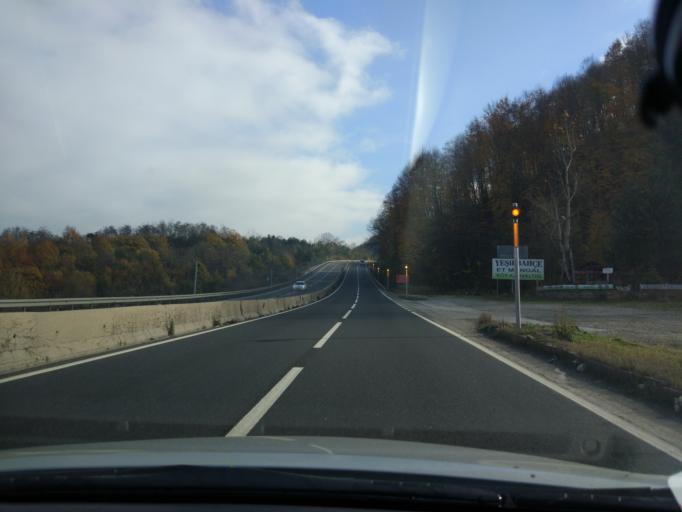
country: TR
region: Duzce
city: Kaynasli
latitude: 40.7579
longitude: 31.3555
